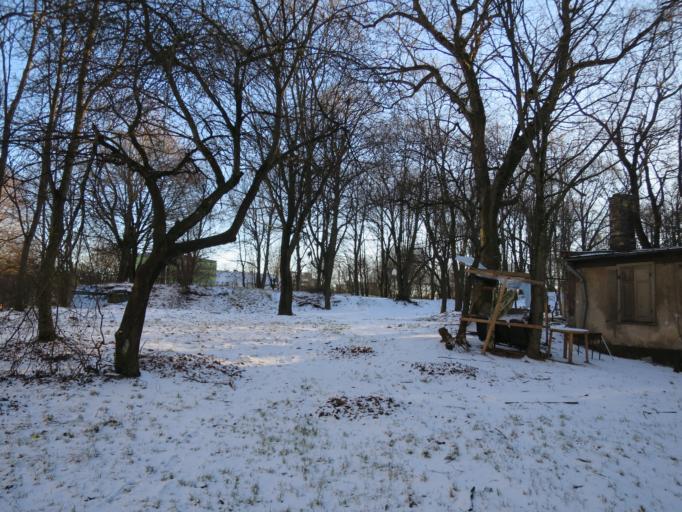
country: LV
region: Riga
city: Jaunciems
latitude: 57.0063
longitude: 24.1221
